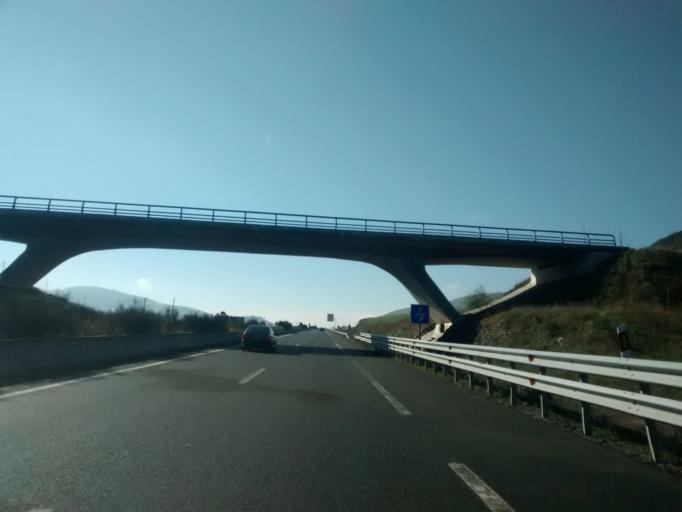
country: ES
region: Cantabria
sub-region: Provincia de Cantabria
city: Pesquera
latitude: 43.0775
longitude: -4.0861
